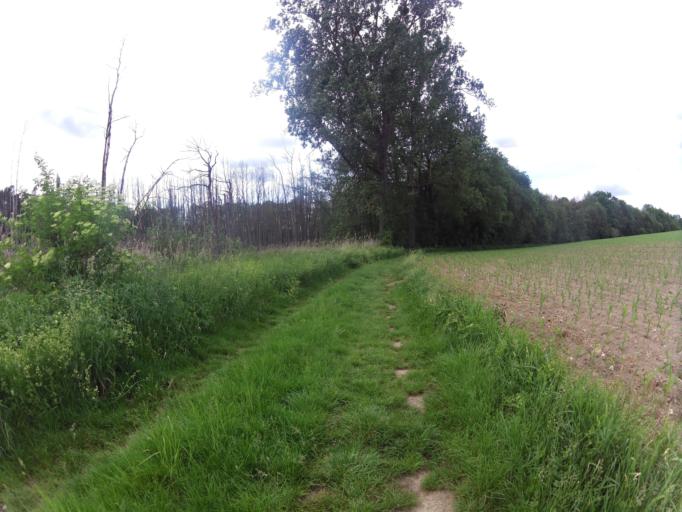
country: DE
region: Bavaria
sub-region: Regierungsbezirk Unterfranken
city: Ochsenfurt
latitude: 49.6949
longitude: 10.0583
